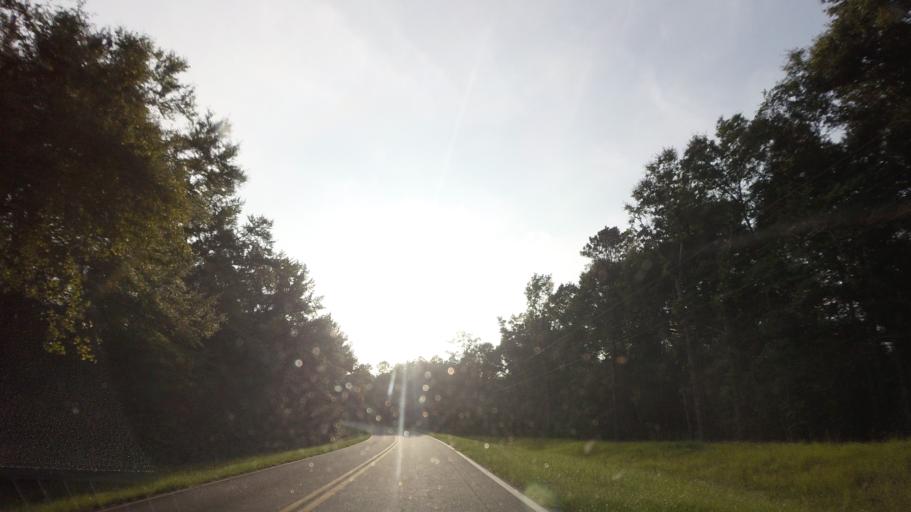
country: US
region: Georgia
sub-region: Wilkinson County
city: Gordon
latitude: 32.8348
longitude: -83.3676
